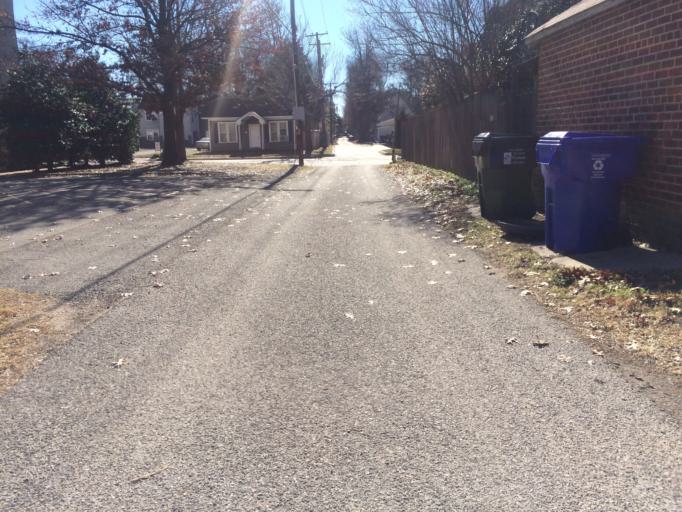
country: US
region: Oklahoma
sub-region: Cleveland County
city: Norman
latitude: 35.2115
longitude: -97.4509
